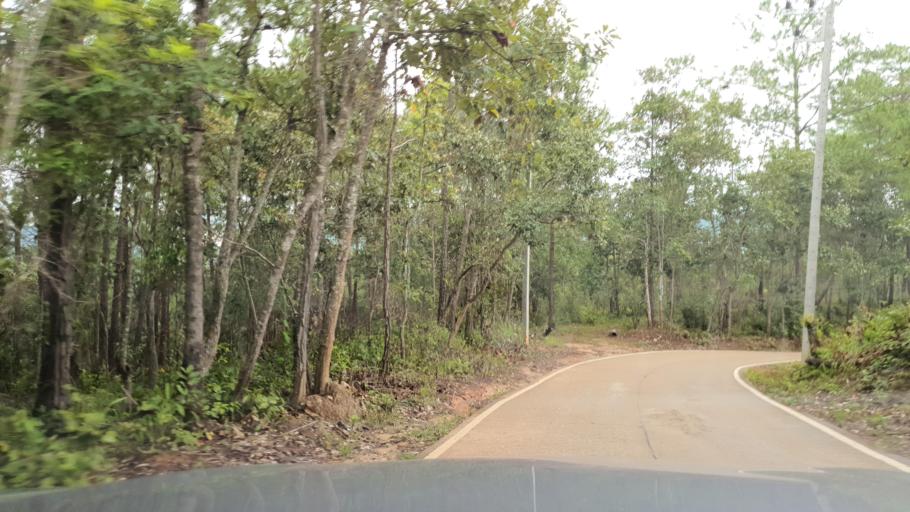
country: TH
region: Chiang Mai
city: Samoeng
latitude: 18.7009
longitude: 98.5705
